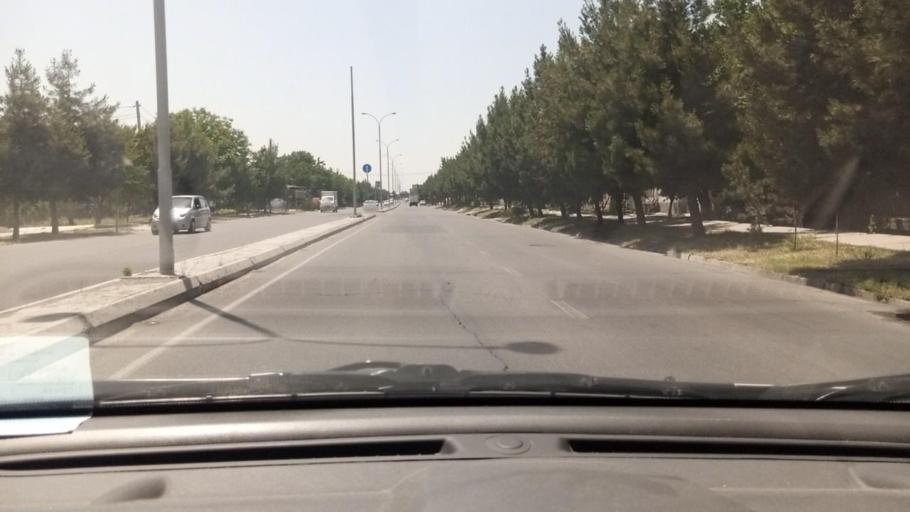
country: UZ
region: Toshkent Shahri
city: Tashkent
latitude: 41.2342
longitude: 69.1872
